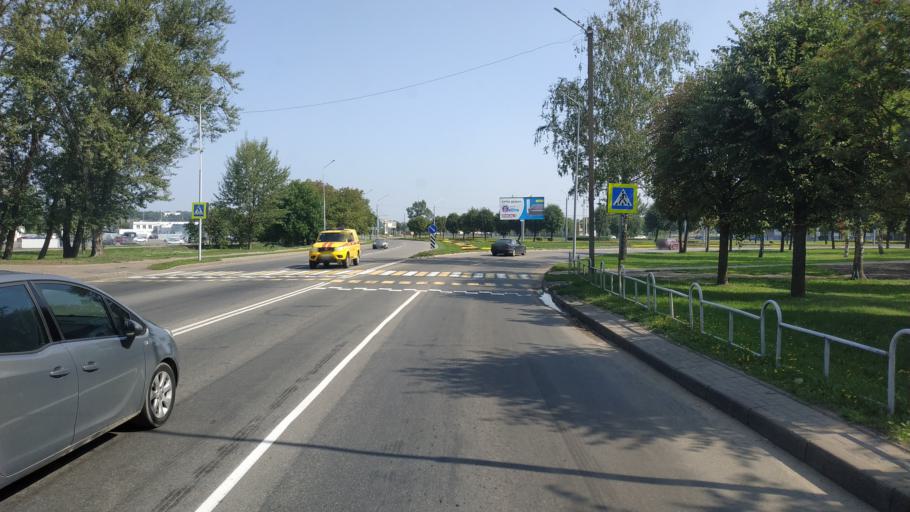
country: BY
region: Mogilev
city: Buynichy
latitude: 53.8756
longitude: 30.3128
